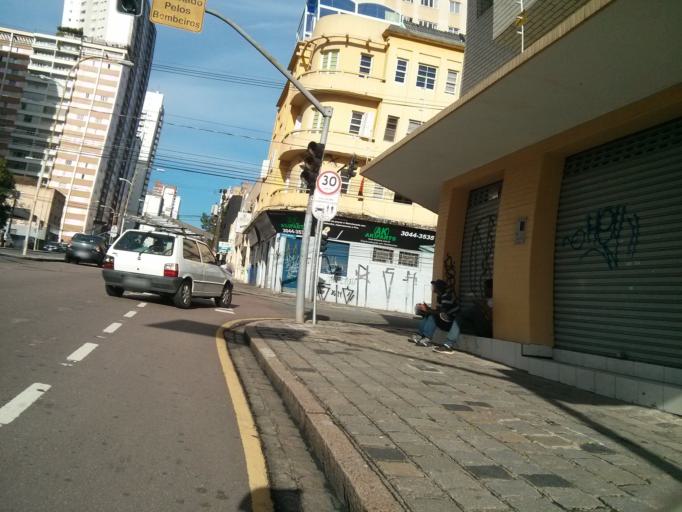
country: BR
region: Parana
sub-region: Curitiba
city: Curitiba
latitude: -25.4405
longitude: -49.2739
